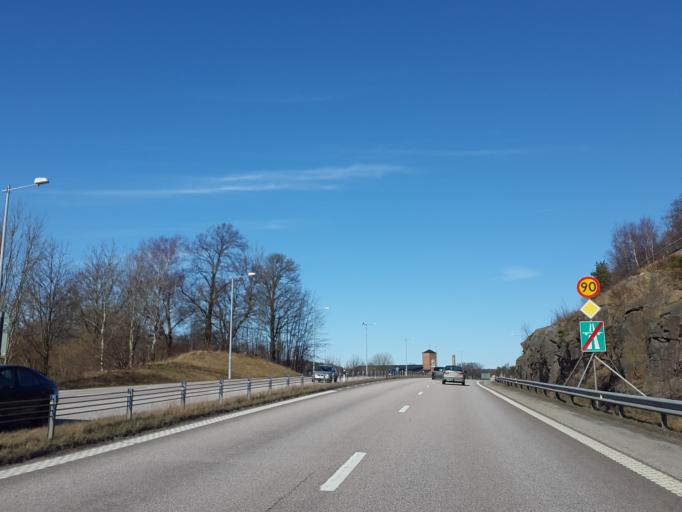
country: SE
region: Vaestra Goetaland
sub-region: Alingsas Kommun
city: Ingared
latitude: 57.8154
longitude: 12.4149
